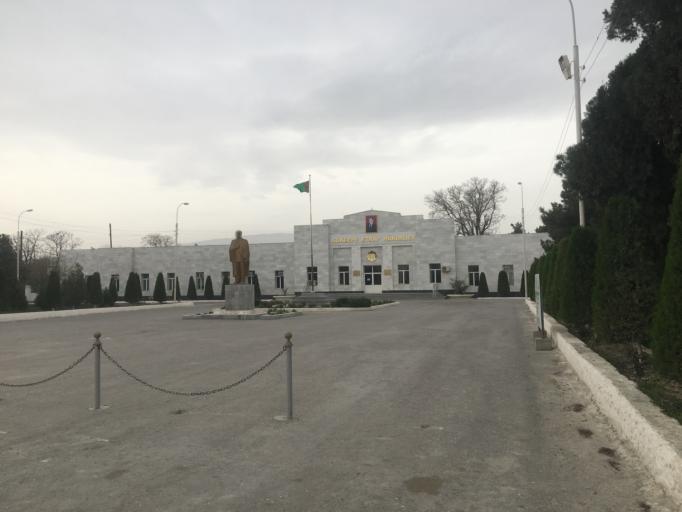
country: TM
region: Ahal
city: Abadan
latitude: 38.1563
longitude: 57.9623
